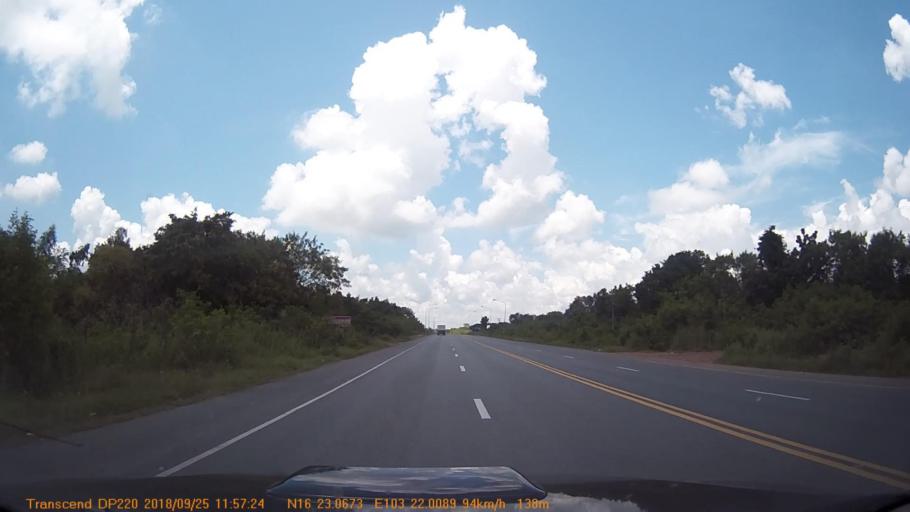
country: TH
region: Kalasin
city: Yang Talat
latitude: 16.3846
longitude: 103.3667
